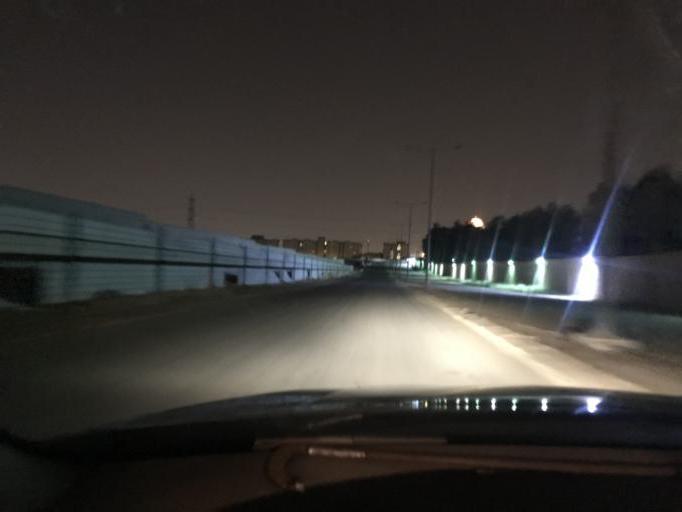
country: SA
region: Ar Riyad
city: Riyadh
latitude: 24.8147
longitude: 46.7161
